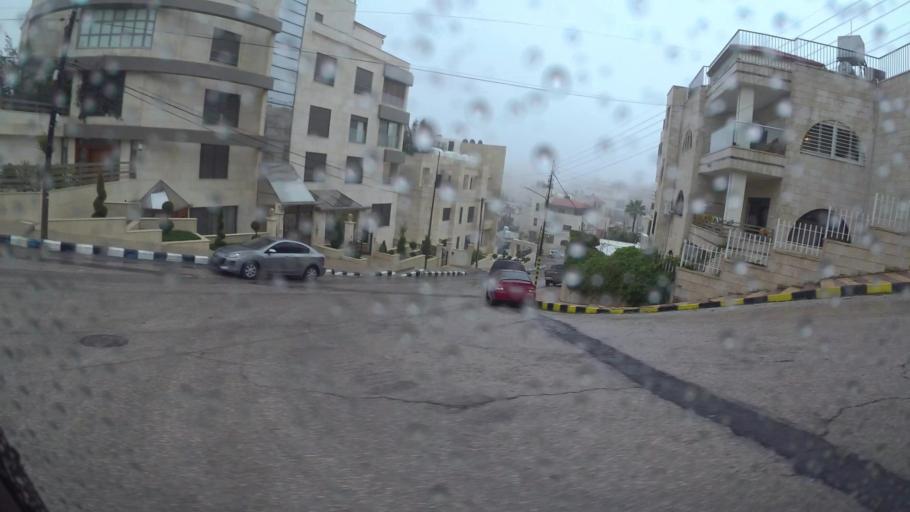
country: JO
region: Amman
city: Wadi as Sir
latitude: 31.9979
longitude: 35.8238
